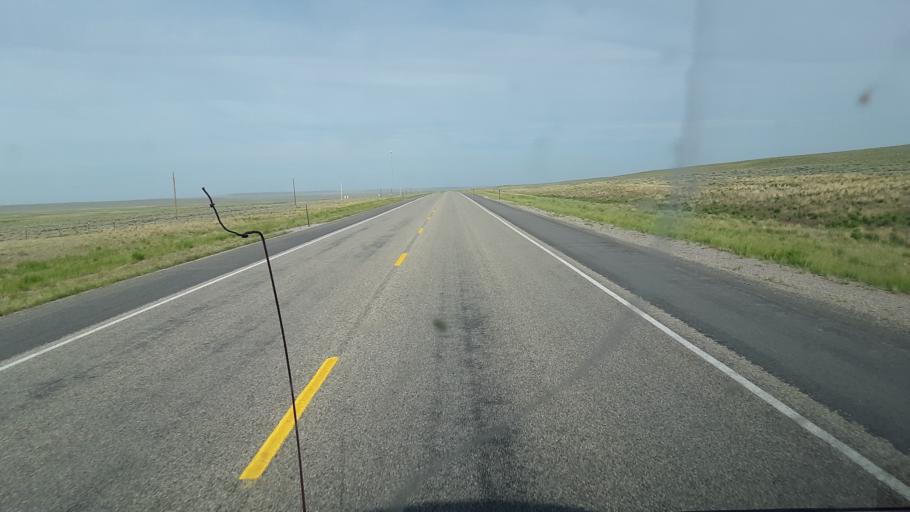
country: US
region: Wyoming
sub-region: Fremont County
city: Riverton
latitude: 43.1397
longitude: -107.5999
